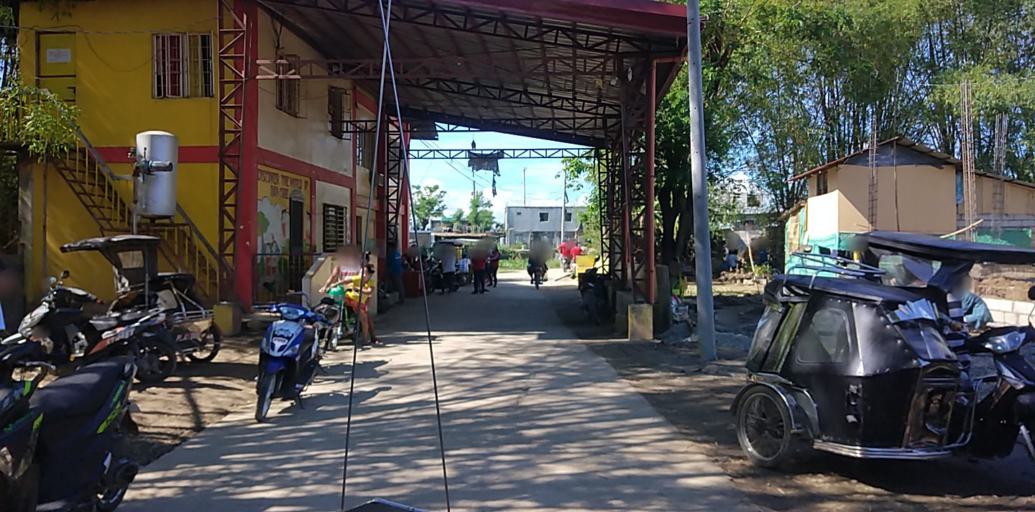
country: PH
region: Central Luzon
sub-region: Province of Pampanga
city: Candating
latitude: 15.1233
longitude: 120.8135
